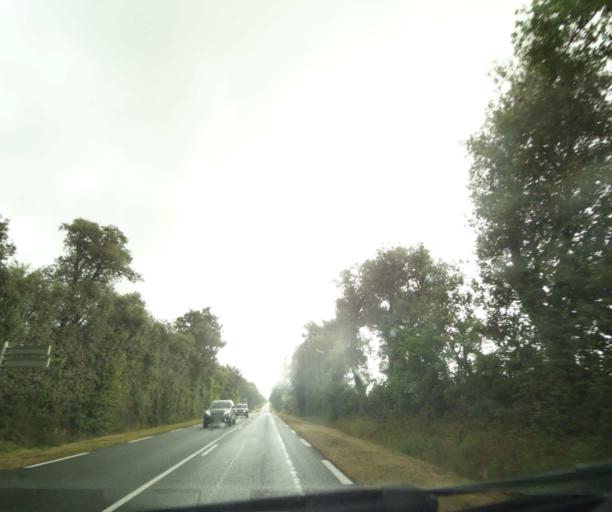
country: FR
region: Pays de la Loire
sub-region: Departement de la Vendee
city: Avrille
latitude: 46.4748
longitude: -1.5267
